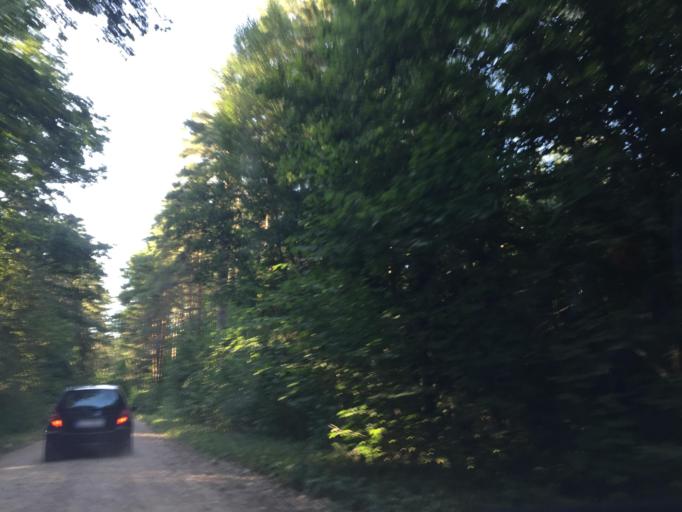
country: LV
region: Kandava
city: Kandava
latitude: 57.0217
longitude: 22.7529
